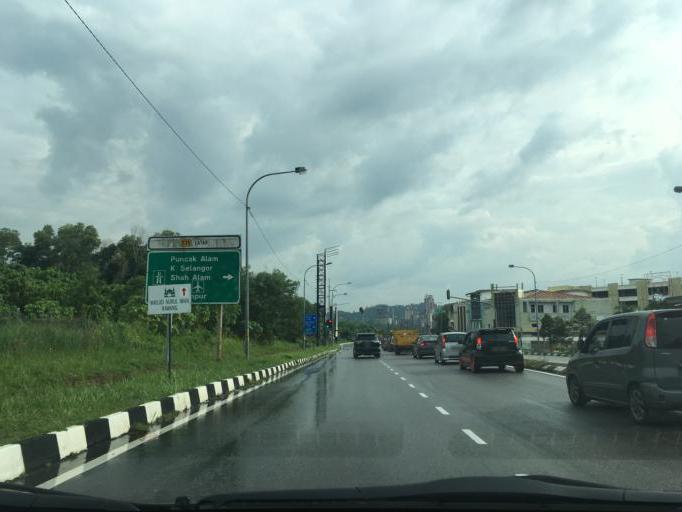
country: MY
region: Selangor
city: Rawang
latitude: 3.3203
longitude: 101.5795
